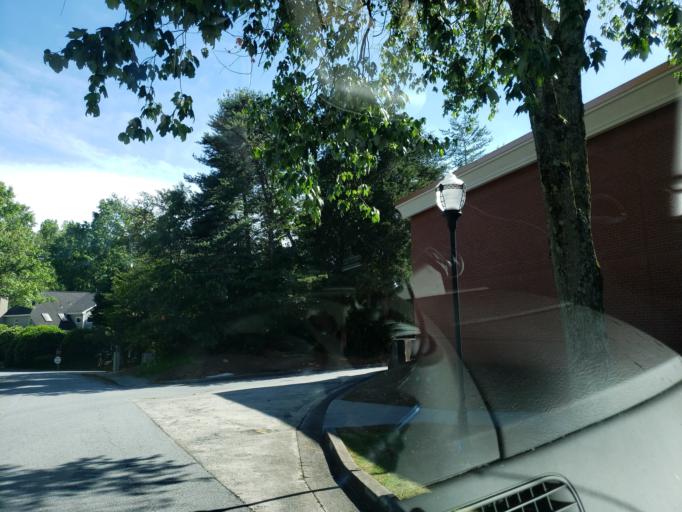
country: US
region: Georgia
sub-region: Fulton County
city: Sandy Springs
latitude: 33.9767
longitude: -84.4173
